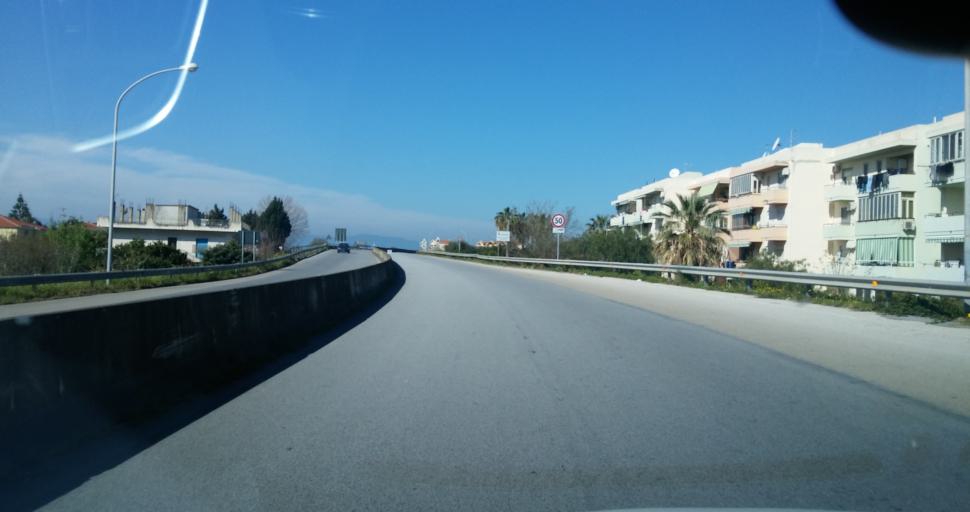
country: IT
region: Sicily
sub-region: Messina
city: Milazzo
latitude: 38.2065
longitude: 15.2427
